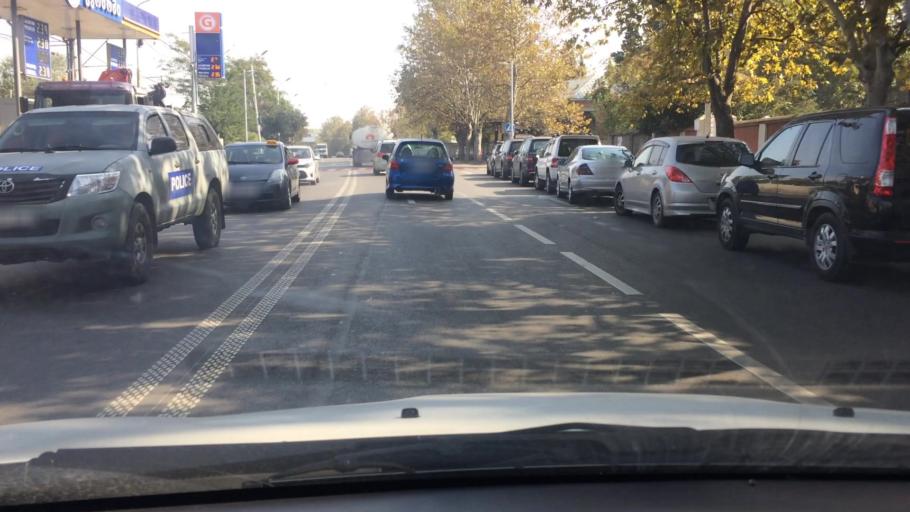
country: GE
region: T'bilisi
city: Tbilisi
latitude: 41.6925
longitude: 44.8264
